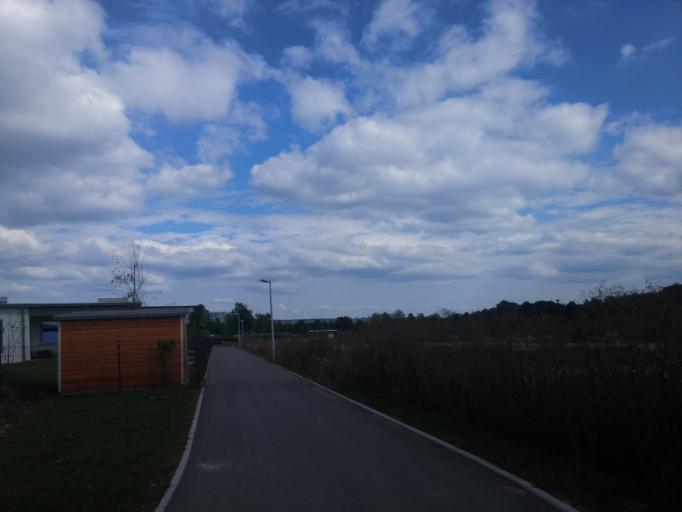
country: DE
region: Bavaria
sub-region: Upper Franconia
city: Coburg
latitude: 50.2802
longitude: 10.9715
